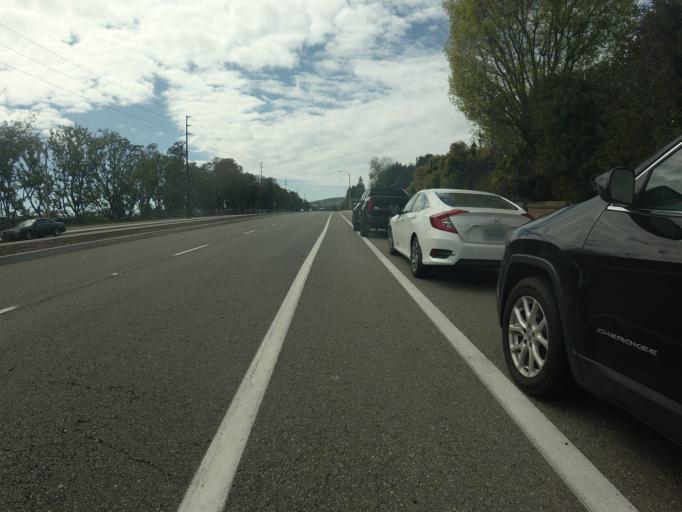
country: US
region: California
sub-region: Orange County
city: Laguna Hills
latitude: 33.5952
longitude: -117.7030
